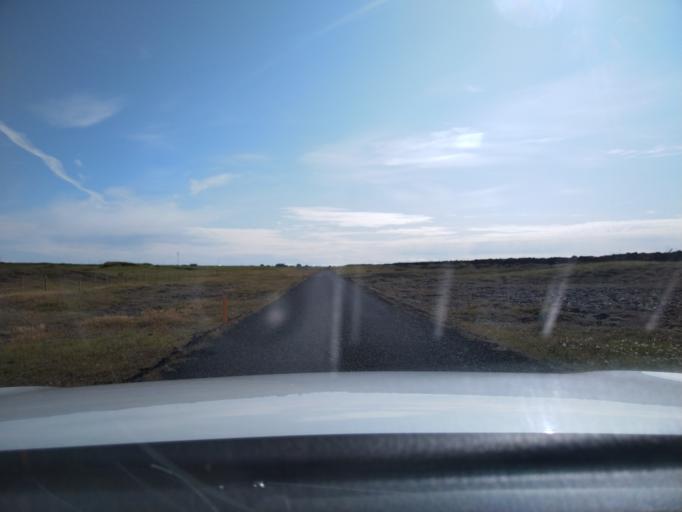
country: IS
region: South
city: THorlakshoefn
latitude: 63.8351
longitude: -21.7038
